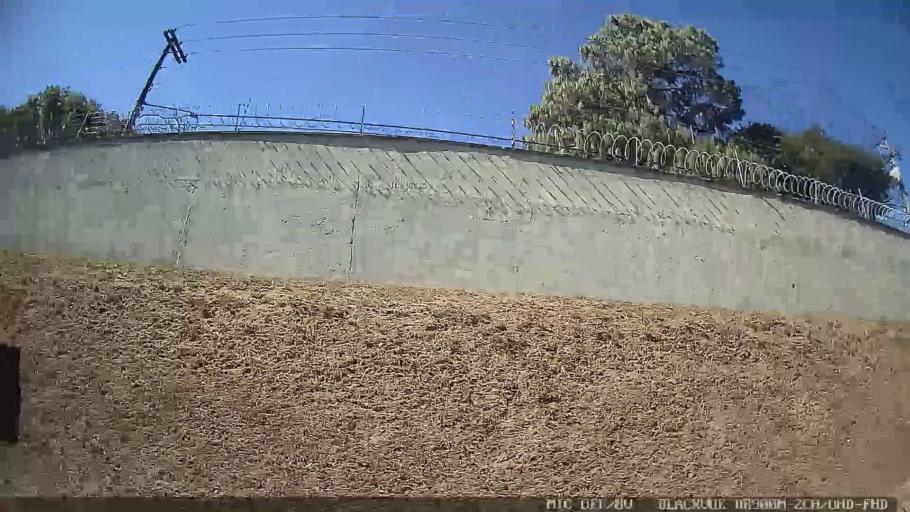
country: BR
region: Sao Paulo
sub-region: Jacarei
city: Jacarei
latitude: -23.2830
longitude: -45.9469
